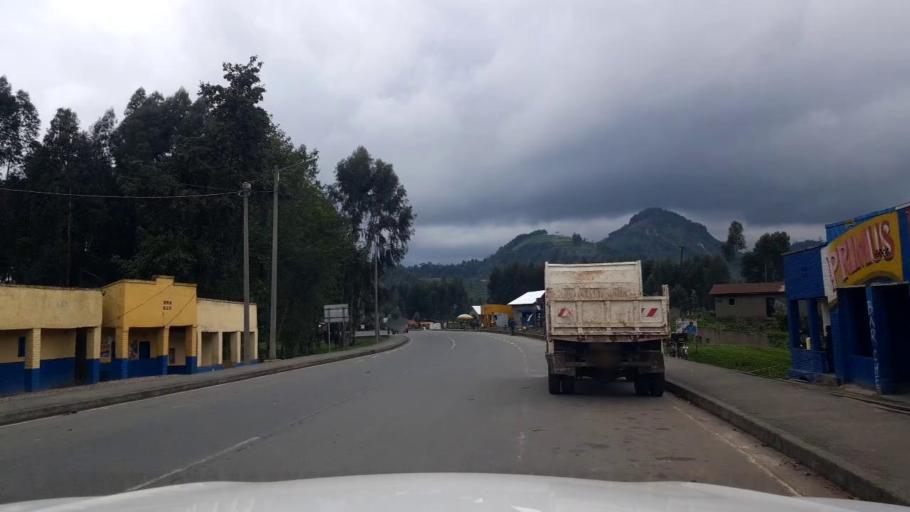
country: RW
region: Northern Province
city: Musanze
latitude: -1.6148
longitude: 29.5016
